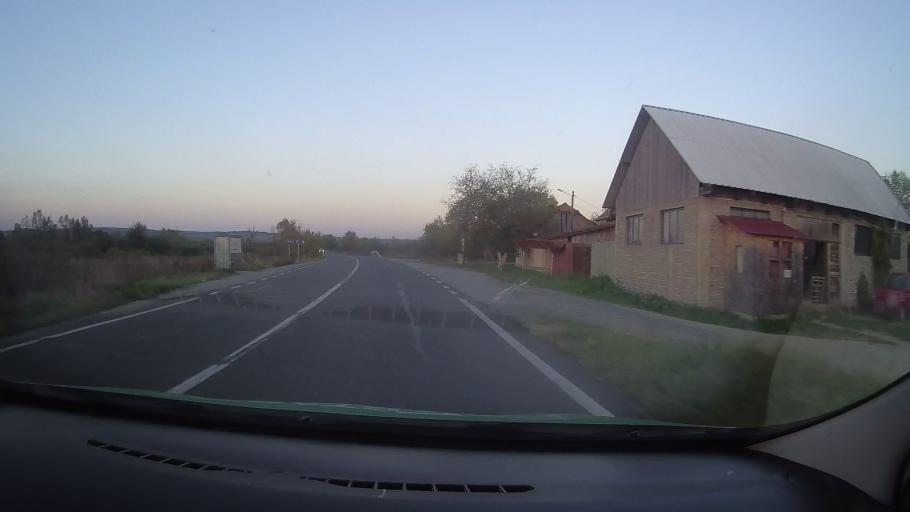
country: RO
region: Timis
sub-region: Comuna Dumbrava
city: Dumbrava
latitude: 45.8378
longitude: 22.1418
